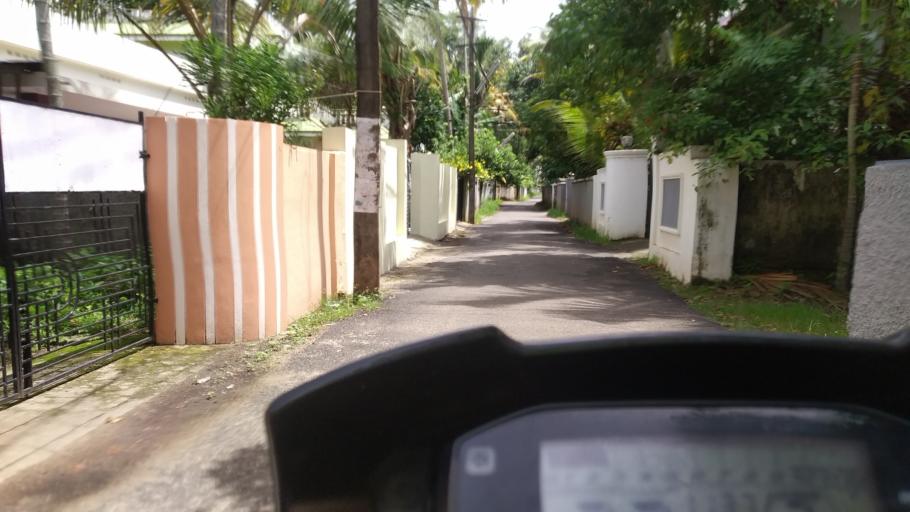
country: IN
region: Kerala
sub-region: Ernakulam
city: Elur
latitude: 10.0821
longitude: 76.2120
